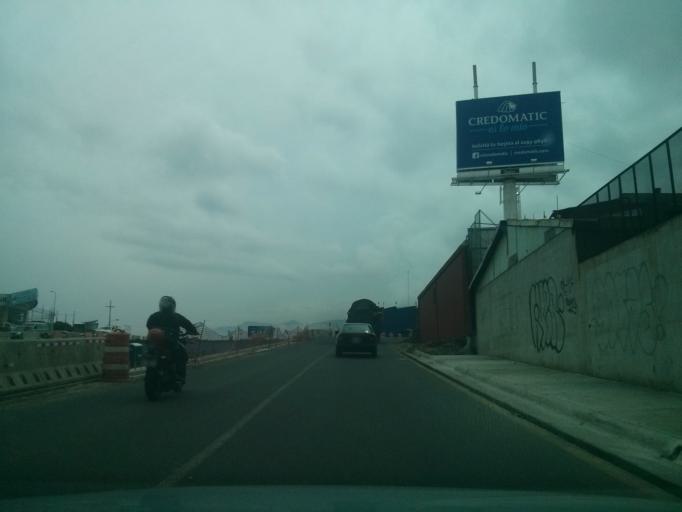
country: CR
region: San Jose
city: San Jose
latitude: 9.9116
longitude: -84.0797
